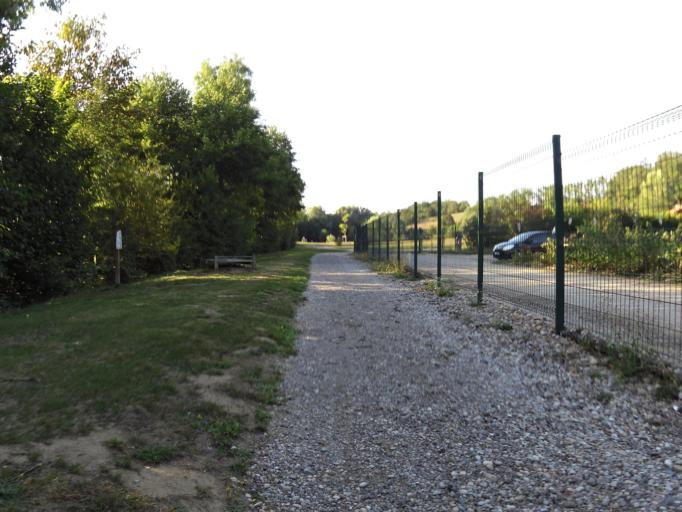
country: FR
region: Rhone-Alpes
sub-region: Departement de l'Ain
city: Meximieux
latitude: 45.9042
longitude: 5.1842
